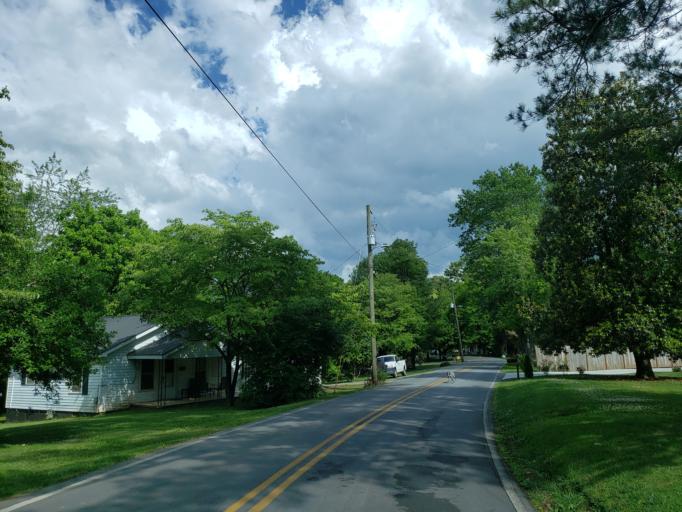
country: US
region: Georgia
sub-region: Pickens County
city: Jasper
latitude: 34.4637
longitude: -84.4255
